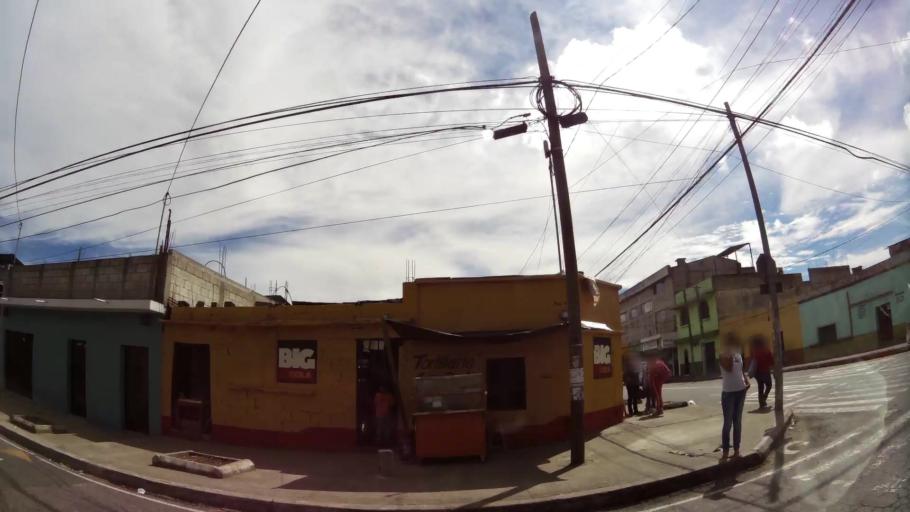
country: GT
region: Guatemala
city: Mixco
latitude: 14.6563
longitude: -90.5805
